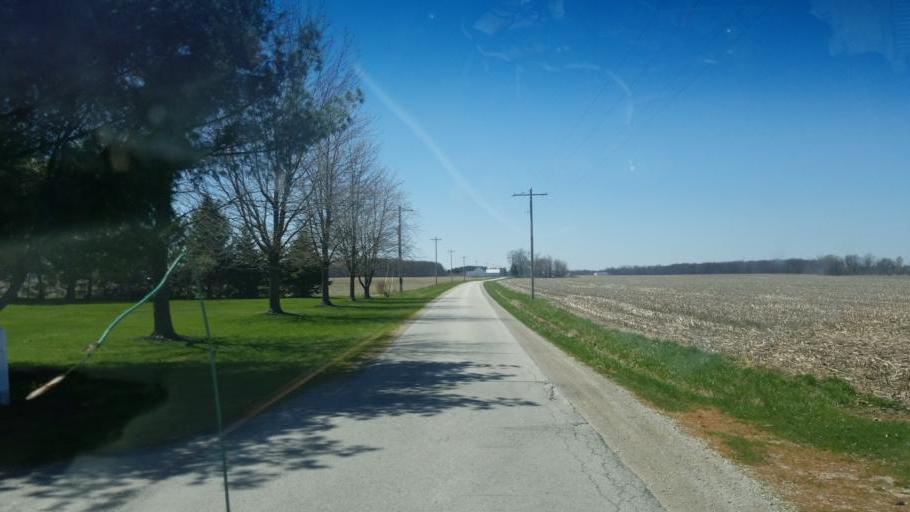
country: US
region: Ohio
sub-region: Huron County
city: Willard
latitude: 41.0444
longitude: -82.8618
